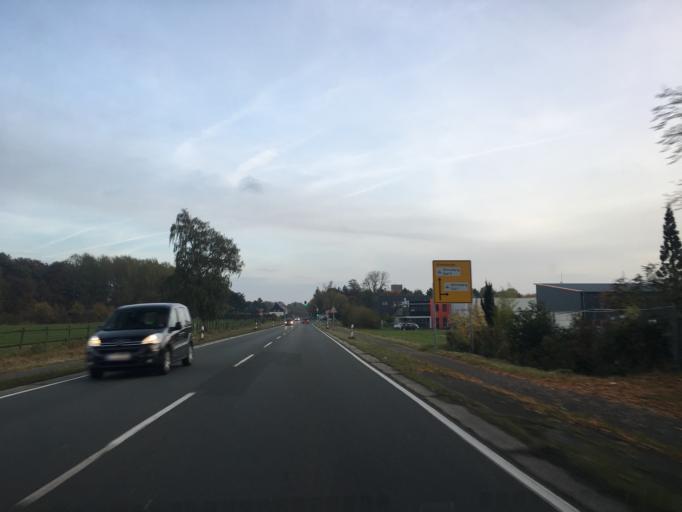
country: DE
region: North Rhine-Westphalia
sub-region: Regierungsbezirk Munster
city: Laer
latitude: 52.0997
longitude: 7.4102
